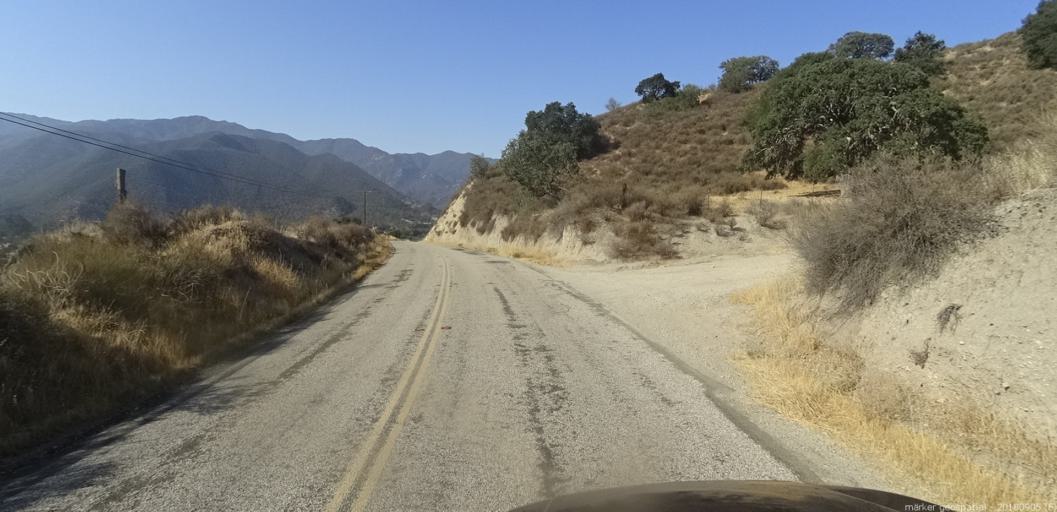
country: US
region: California
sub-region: Monterey County
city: Greenfield
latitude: 36.2637
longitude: -121.4148
